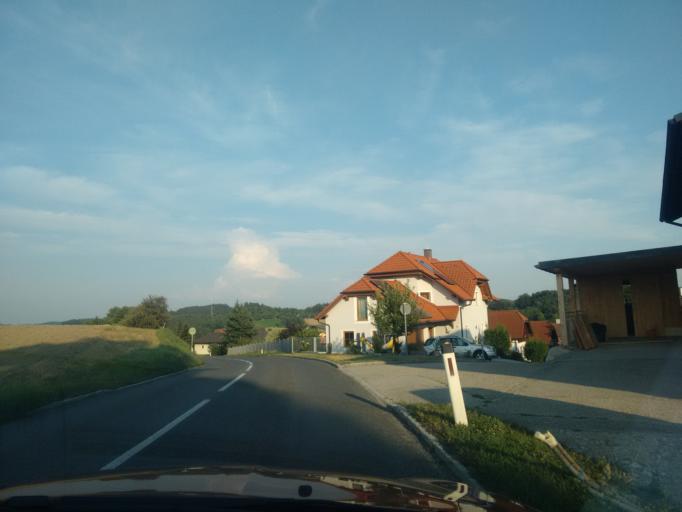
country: AT
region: Upper Austria
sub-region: Politischer Bezirk Vocklabruck
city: Niederthalheim
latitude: 48.1409
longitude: 13.7236
